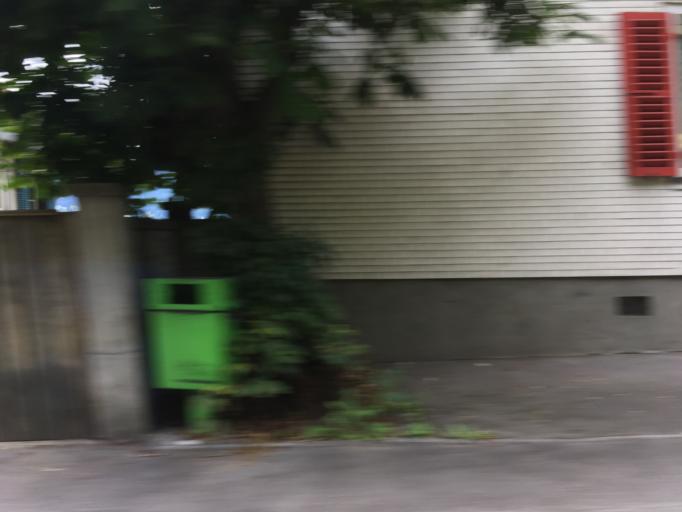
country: CH
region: Bern
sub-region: Thun District
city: Hilterfingen
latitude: 46.7326
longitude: 7.6623
